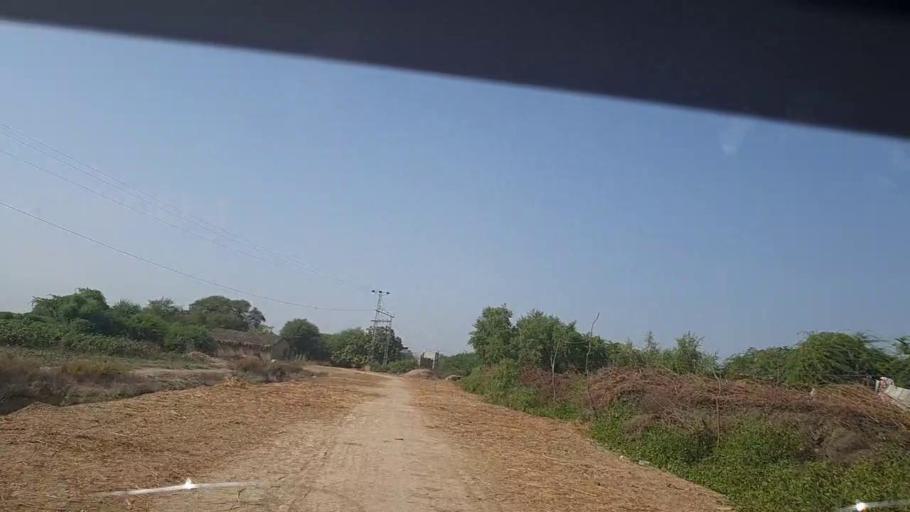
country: PK
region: Sindh
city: Rajo Khanani
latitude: 24.9580
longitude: 68.8980
